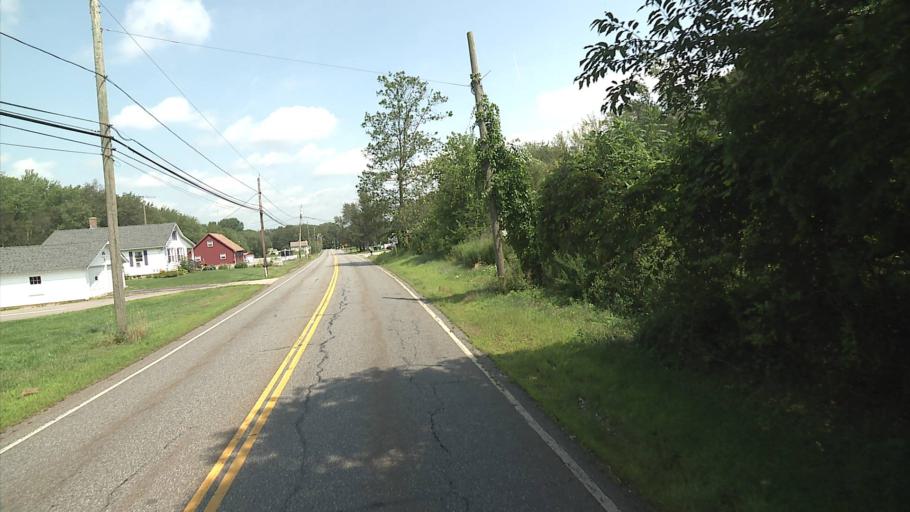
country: US
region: Connecticut
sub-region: New London County
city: Montville Center
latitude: 41.5026
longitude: -72.1657
